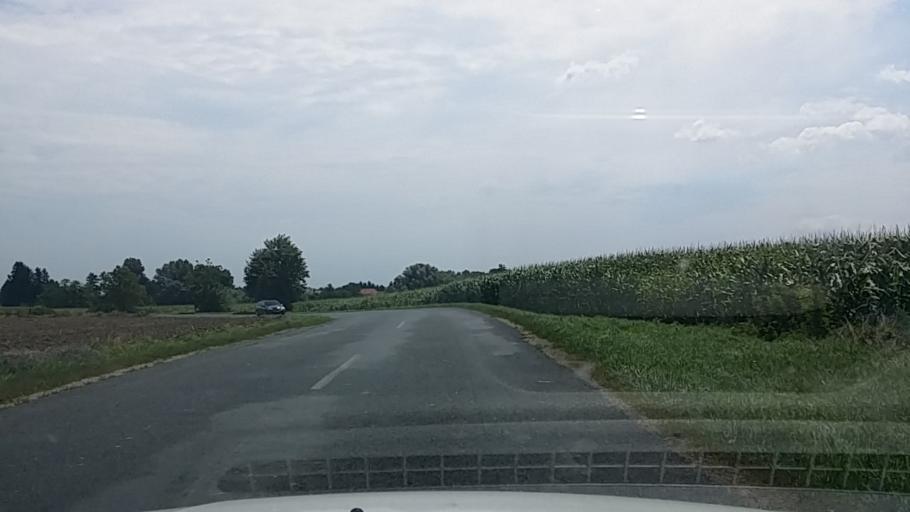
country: HR
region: Medimurska
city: Kotoriba
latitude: 46.3915
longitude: 16.8184
